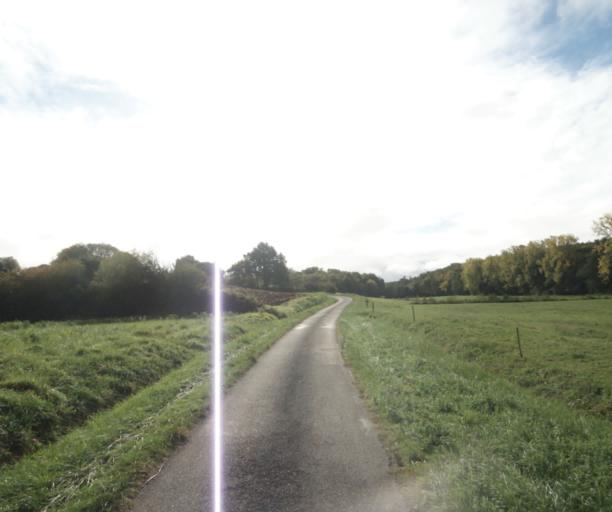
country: FR
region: Midi-Pyrenees
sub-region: Departement du Gers
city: Cazaubon
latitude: 43.8588
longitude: -0.0964
